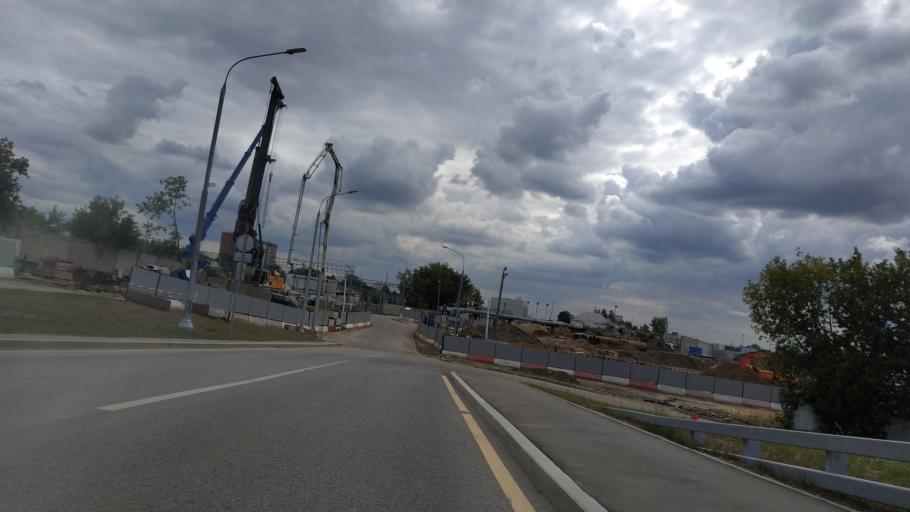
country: RU
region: Moscow
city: Ryazanskiy
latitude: 55.7451
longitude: 37.7342
